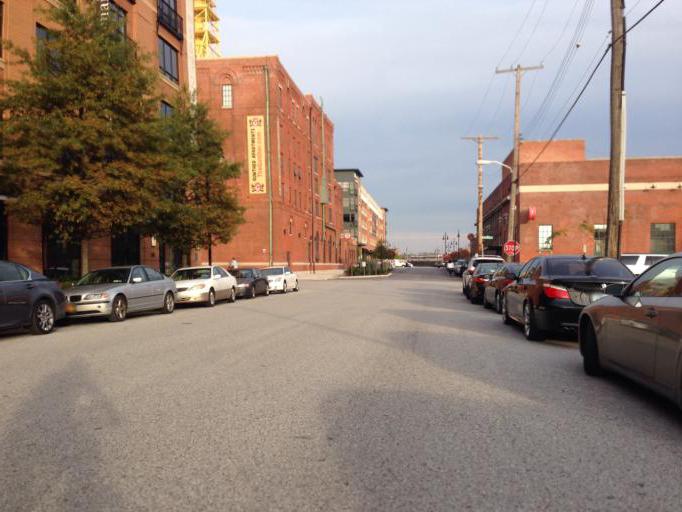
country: US
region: Maryland
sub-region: City of Baltimore
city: Baltimore
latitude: 39.2785
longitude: -76.5672
